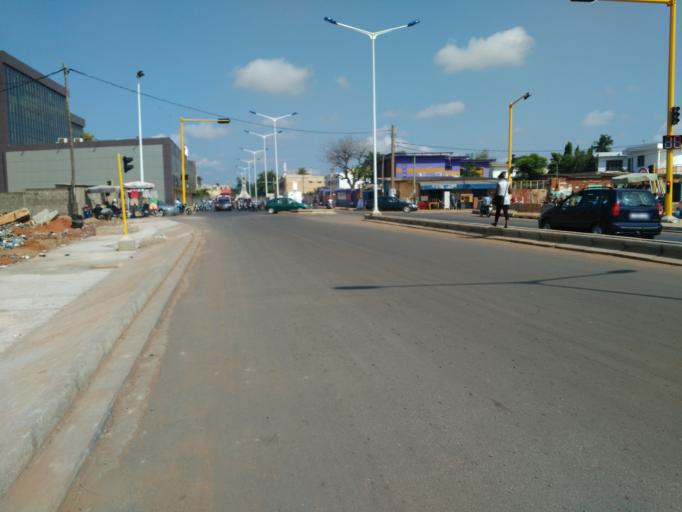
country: TG
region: Maritime
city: Lome
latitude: 6.1494
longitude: 1.2323
